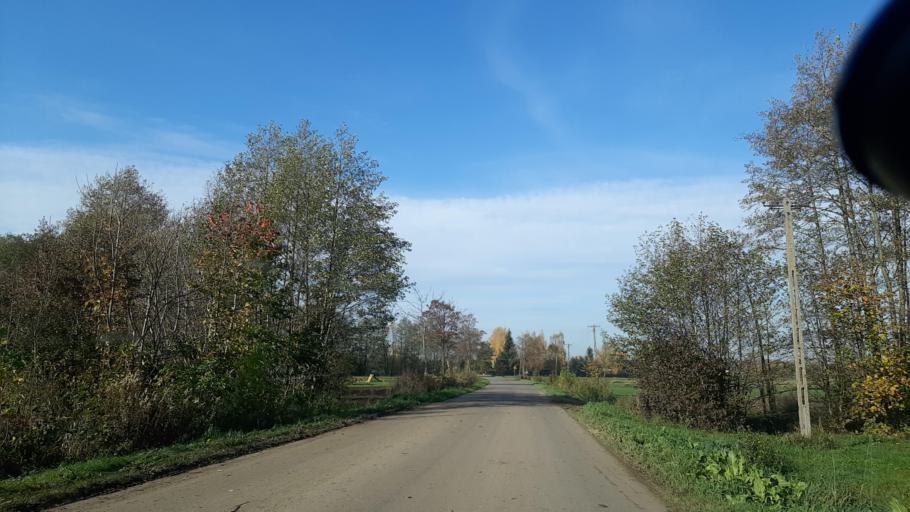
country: PL
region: Lublin Voivodeship
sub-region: Powiat lubelski
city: Jastkow
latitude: 51.3419
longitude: 22.4641
